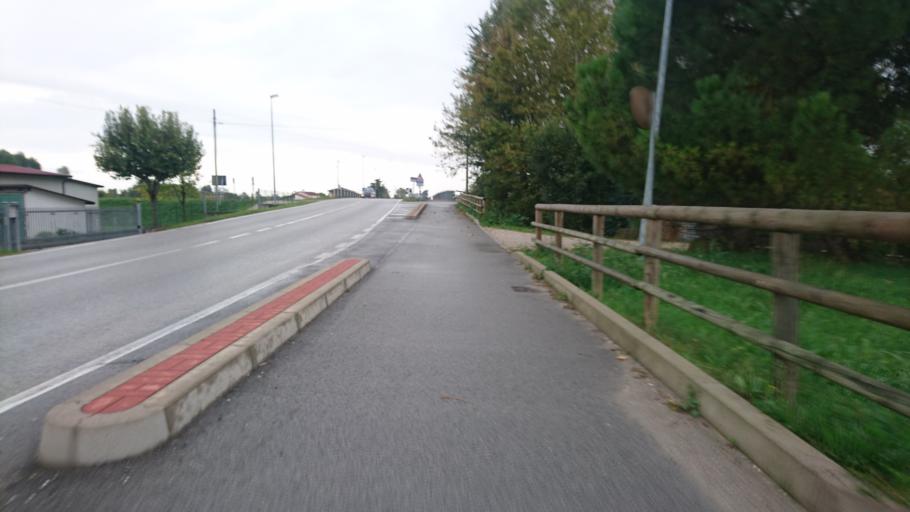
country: IT
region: Veneto
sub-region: Provincia di Padova
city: Veggiano
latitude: 45.4453
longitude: 11.7211
